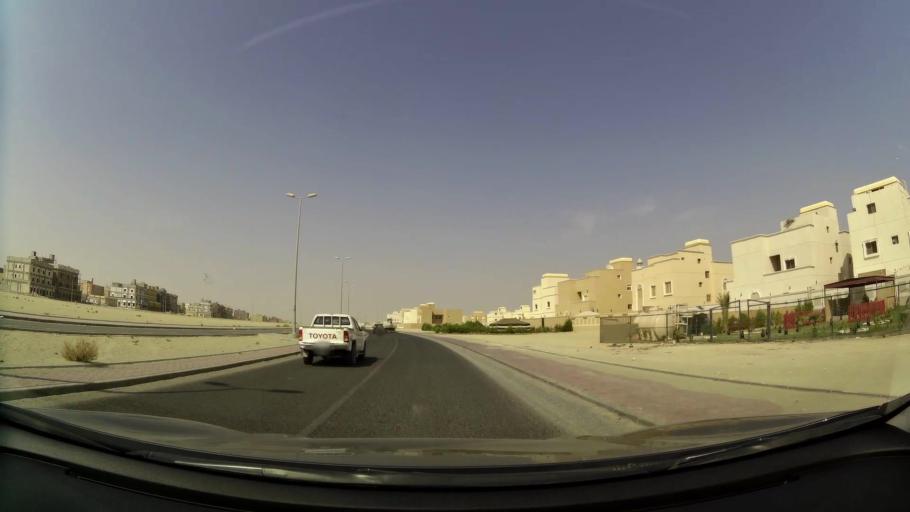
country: KW
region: Al Ahmadi
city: Al Wafrah
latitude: 28.7963
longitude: 48.0637
